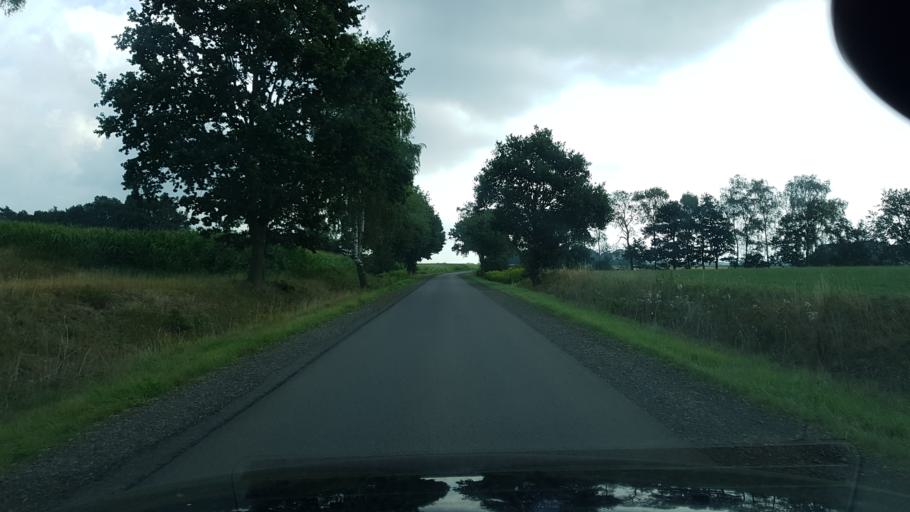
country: DE
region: Lower Saxony
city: Sulingen
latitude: 52.6786
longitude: 8.7566
